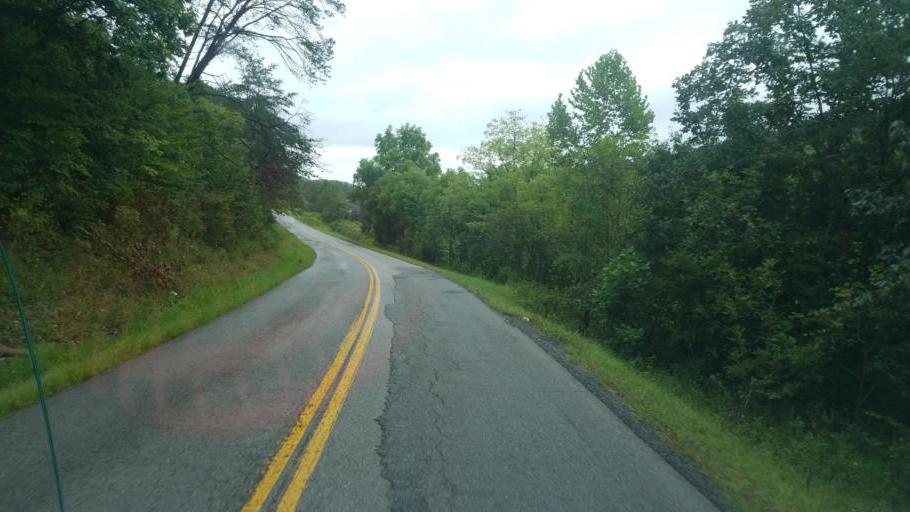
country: US
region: Kentucky
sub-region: Rowan County
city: Morehead
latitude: 38.3636
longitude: -83.5348
